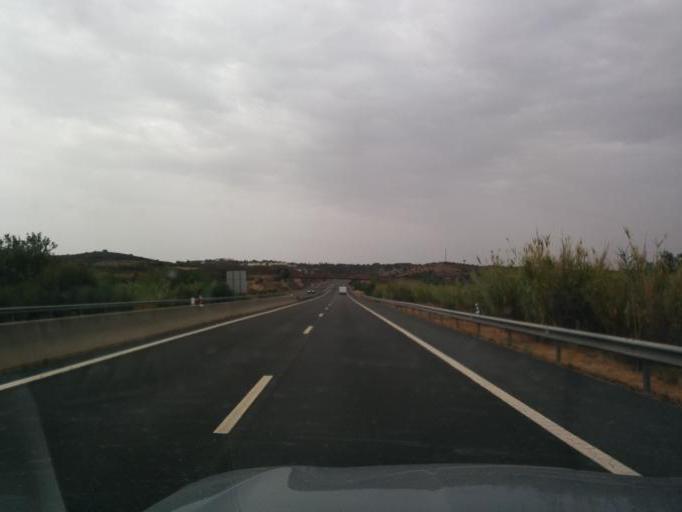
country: PT
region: Faro
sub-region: Castro Marim
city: Castro Marim
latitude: 37.2184
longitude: -7.4798
